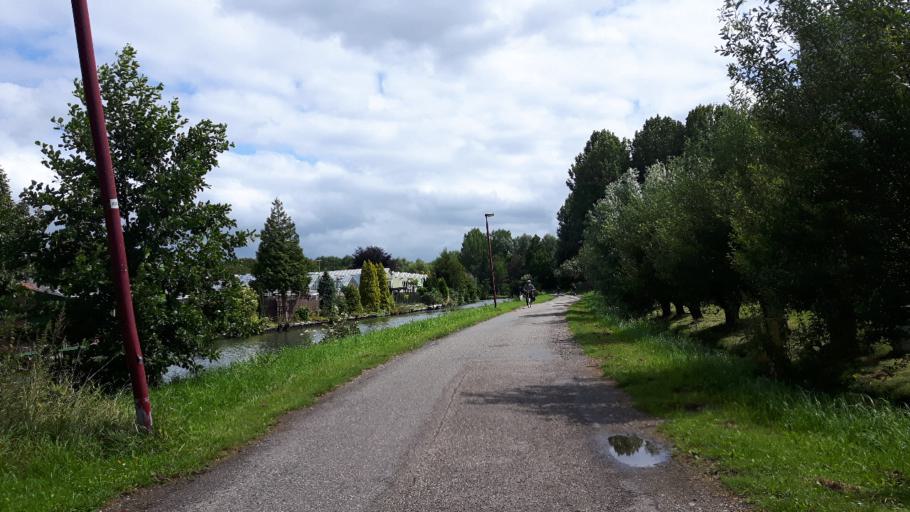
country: NL
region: Utrecht
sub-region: Gemeente Nieuwegein
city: Nieuwegein
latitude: 52.0167
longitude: 5.0724
